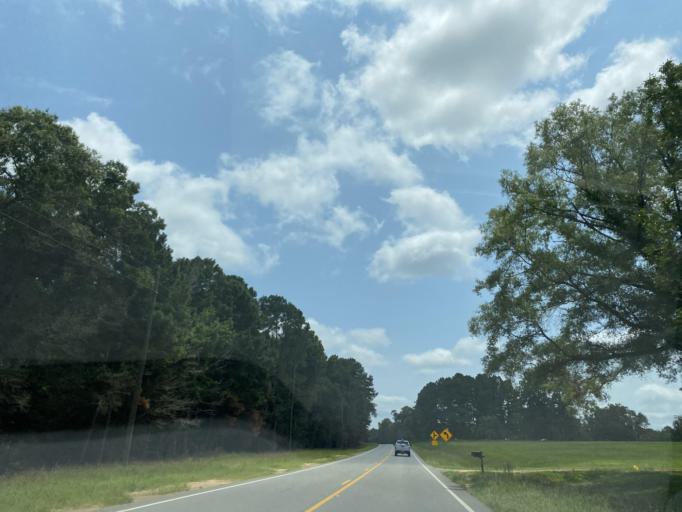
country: US
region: Georgia
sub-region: Jeff Davis County
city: Hazlehurst
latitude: 31.7769
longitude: -82.5625
